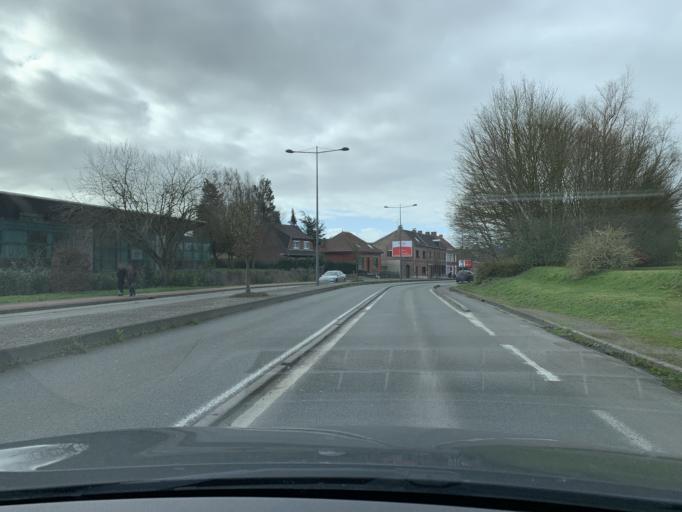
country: FR
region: Nord-Pas-de-Calais
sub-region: Departement du Nord
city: Waziers
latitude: 50.3874
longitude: 3.1005
